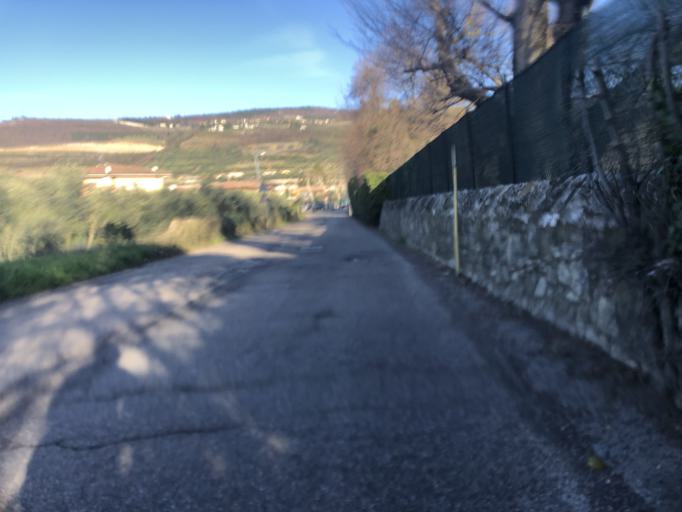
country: IT
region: Veneto
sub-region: Provincia di Verona
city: Fumane
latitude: 45.5345
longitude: 10.8801
